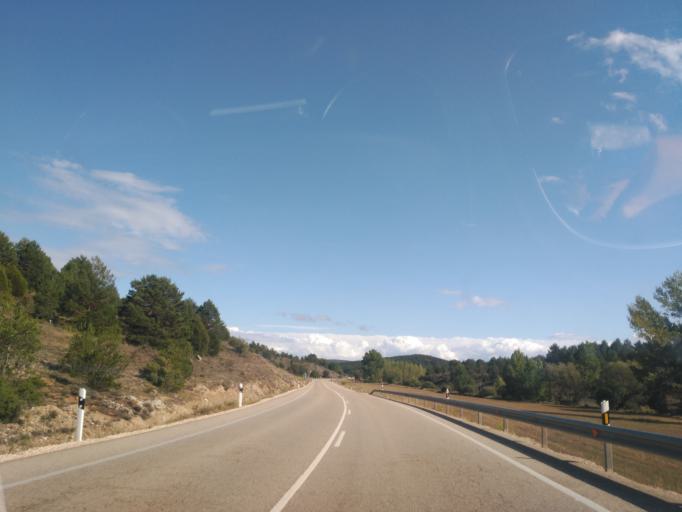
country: ES
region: Castille and Leon
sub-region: Provincia de Burgos
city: Rabanera del Pinar
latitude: 41.8736
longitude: -3.2205
